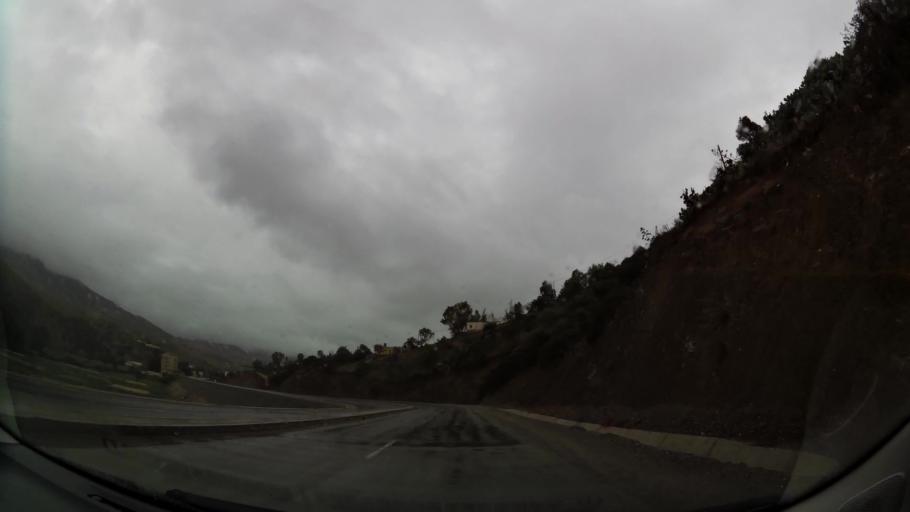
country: MA
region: Taza-Al Hoceima-Taounate
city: Imzourene
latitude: 35.0172
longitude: -3.8199
